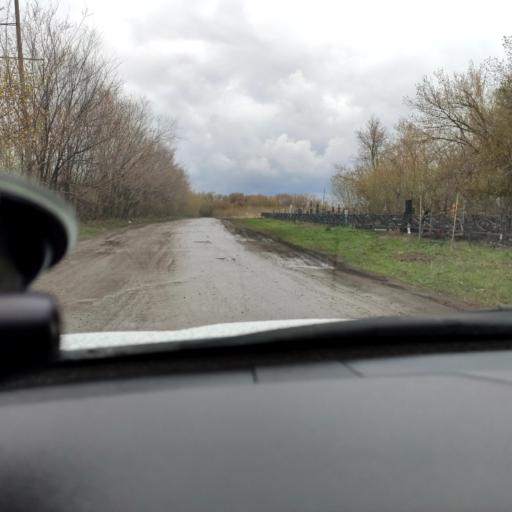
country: RU
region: Samara
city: Smyshlyayevka
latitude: 53.2670
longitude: 50.4863
